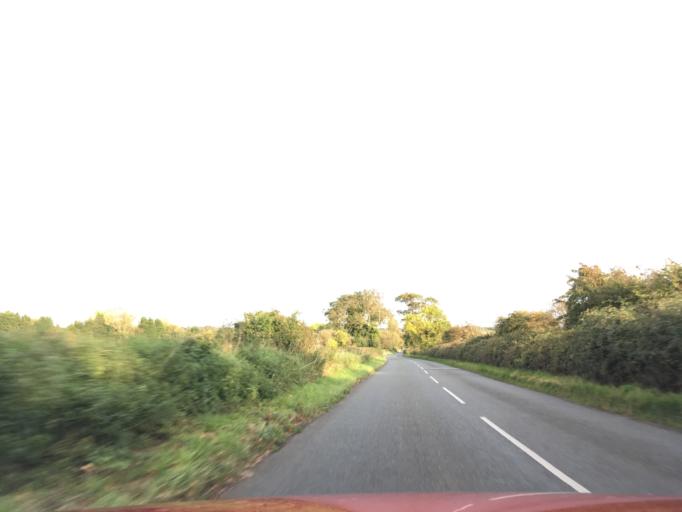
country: GB
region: England
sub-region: South Gloucestershire
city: Almondsbury
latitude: 51.5931
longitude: -2.5934
